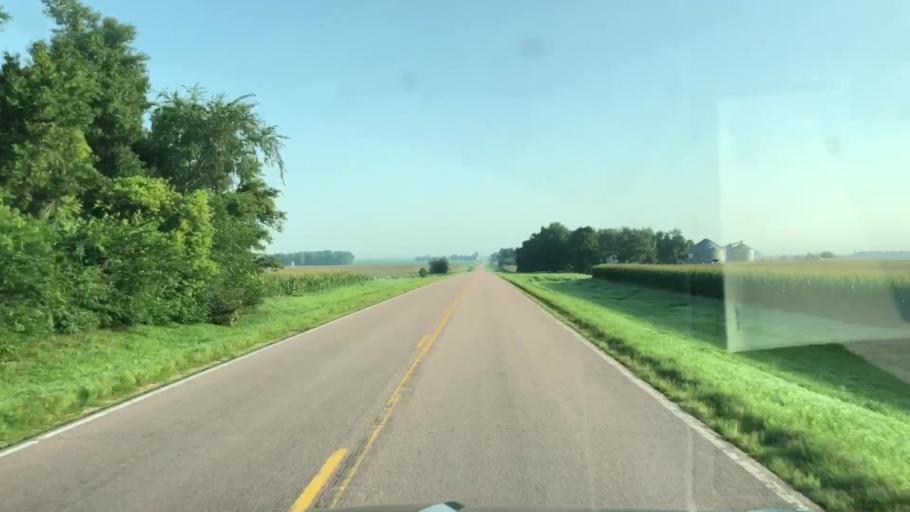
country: US
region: Iowa
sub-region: Lyon County
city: George
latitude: 43.2910
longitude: -95.9995
